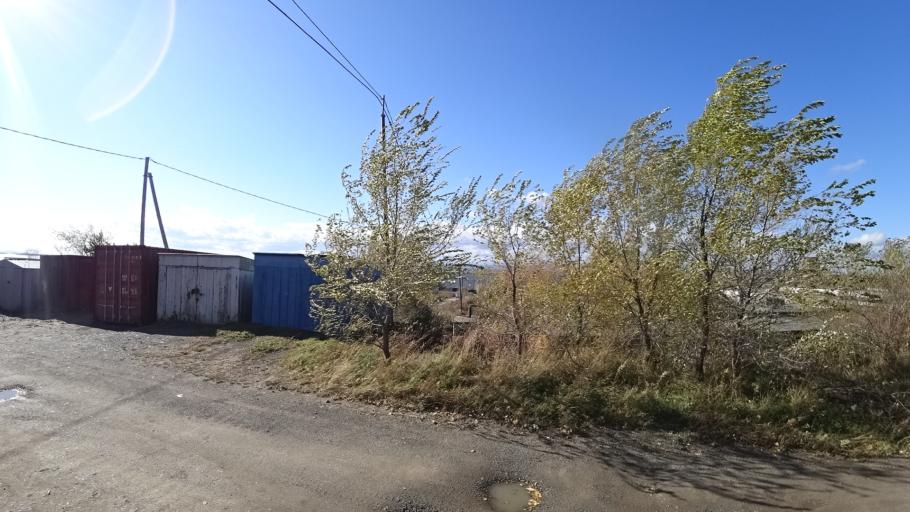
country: RU
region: Khabarovsk Krai
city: Amursk
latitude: 50.2170
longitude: 136.8893
